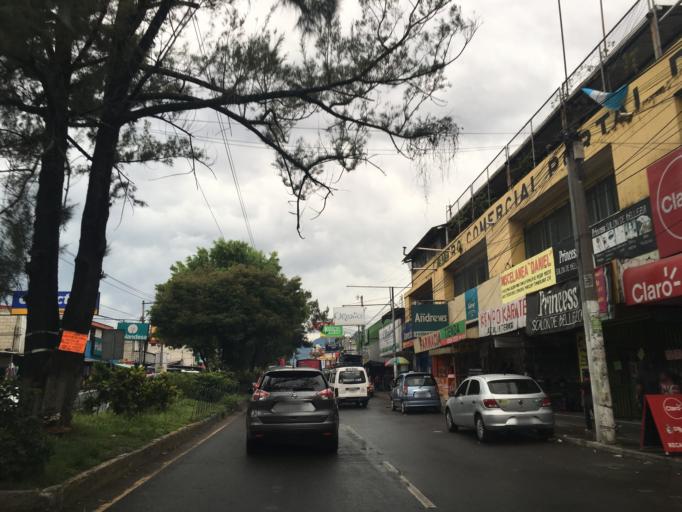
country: GT
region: Guatemala
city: Petapa
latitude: 14.5212
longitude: -90.5414
